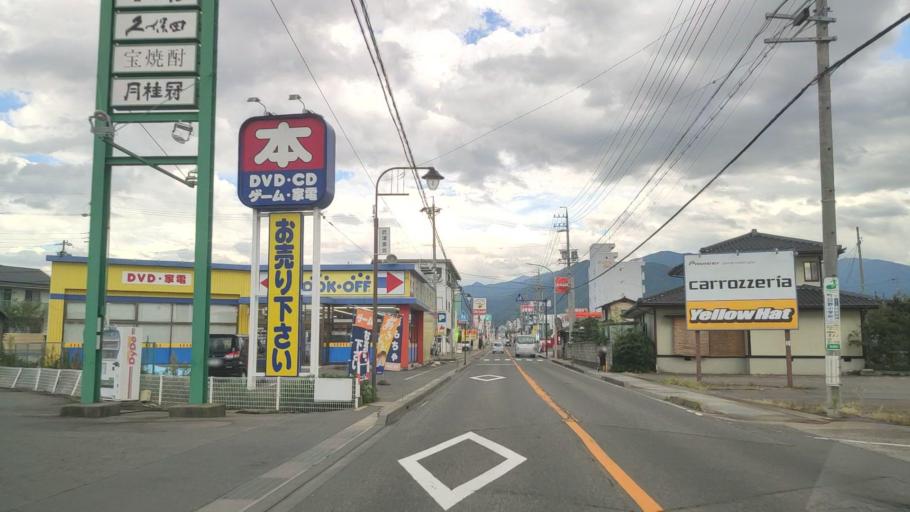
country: JP
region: Nagano
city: Suzaka
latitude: 36.6547
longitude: 138.2894
